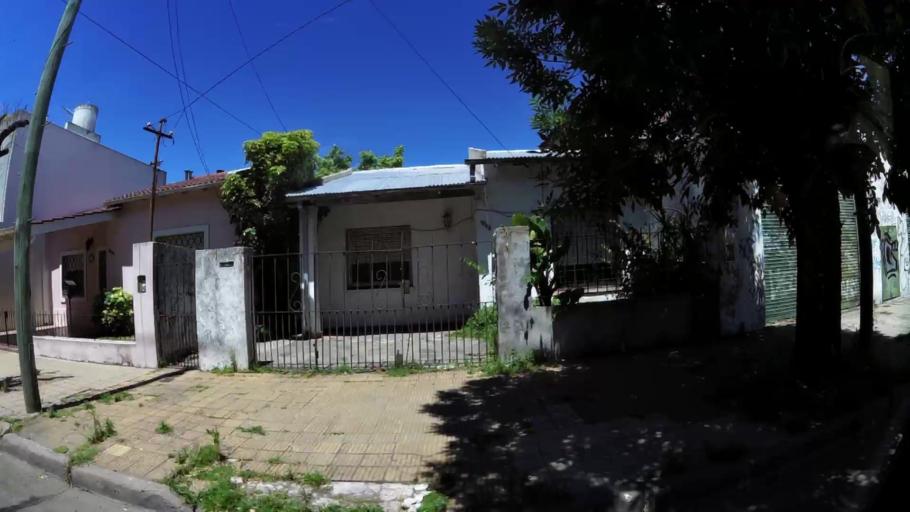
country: AR
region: Buenos Aires
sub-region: Partido de San Isidro
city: San Isidro
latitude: -34.4933
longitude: -58.5144
